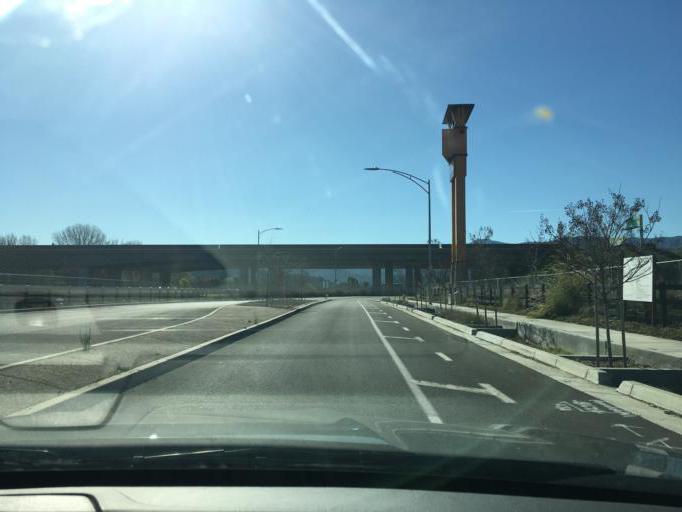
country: US
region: California
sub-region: Santa Clara County
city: Seven Trees
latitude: 37.2577
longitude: -121.8706
